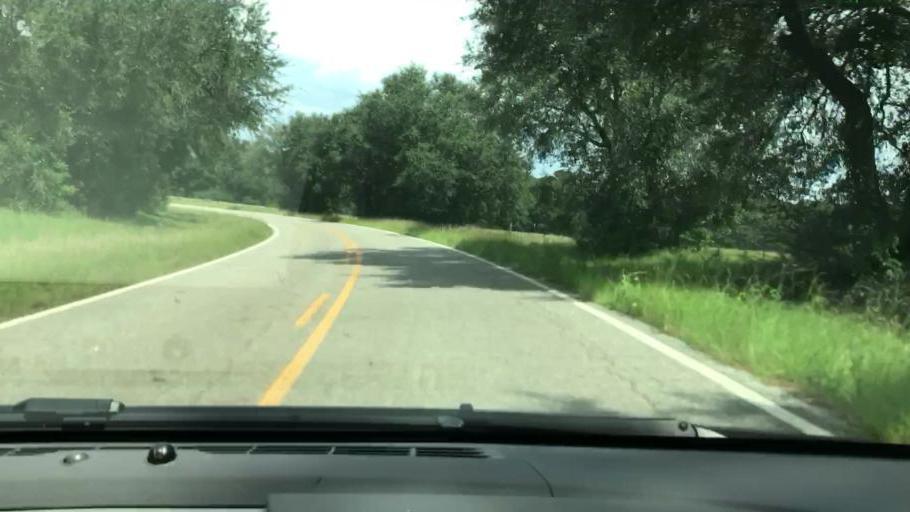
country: US
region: Georgia
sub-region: Early County
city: Blakely
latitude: 31.2226
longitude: -85.0017
